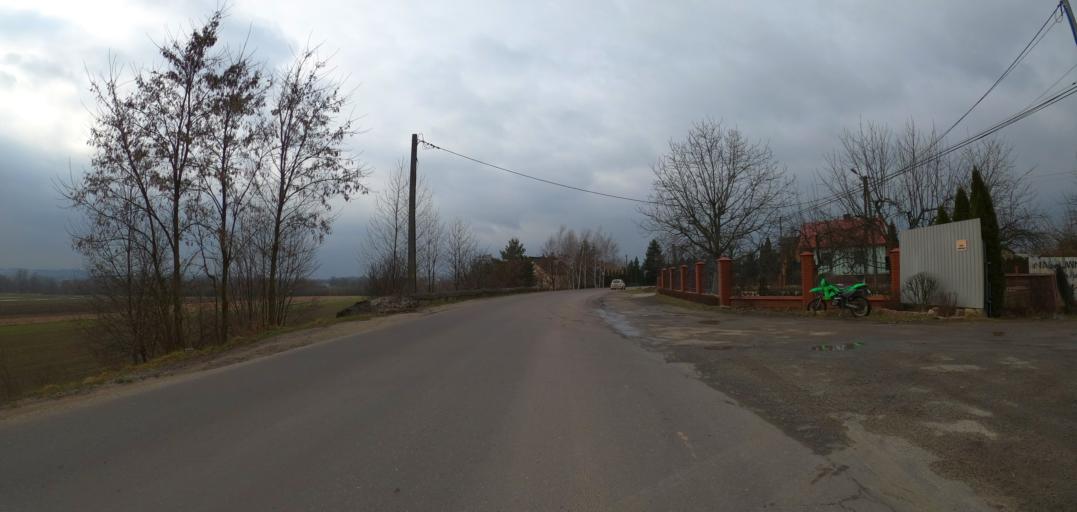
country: PL
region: Subcarpathian Voivodeship
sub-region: Powiat debicki
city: Pilzno
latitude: 49.9875
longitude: 21.3158
